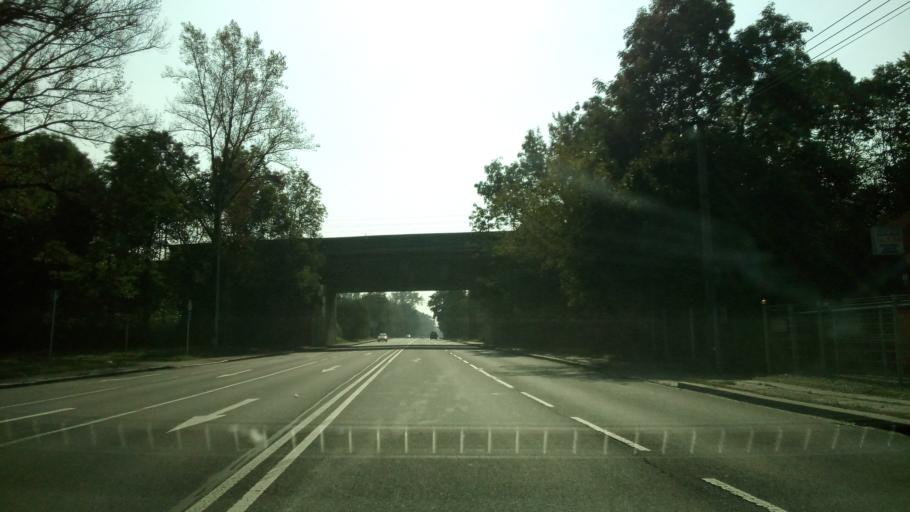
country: CZ
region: Moravskoslezsky
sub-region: Okres Ostrava-Mesto
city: Ostrava
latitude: 49.8029
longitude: 18.2907
